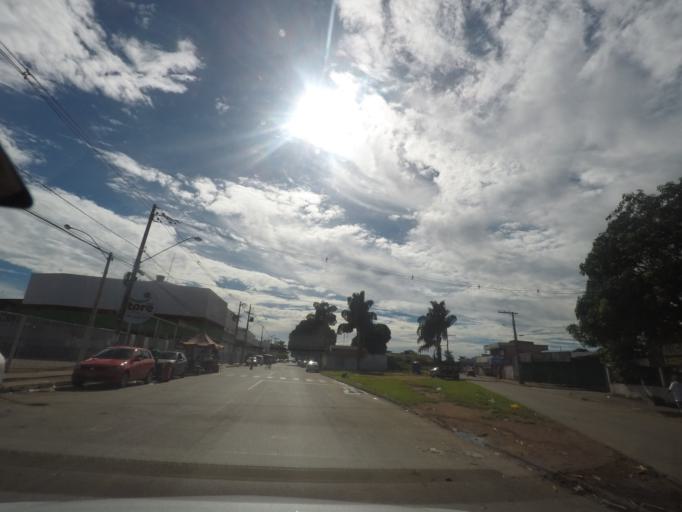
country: BR
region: Goias
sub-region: Aparecida De Goiania
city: Aparecida de Goiania
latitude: -16.8241
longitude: -49.2850
